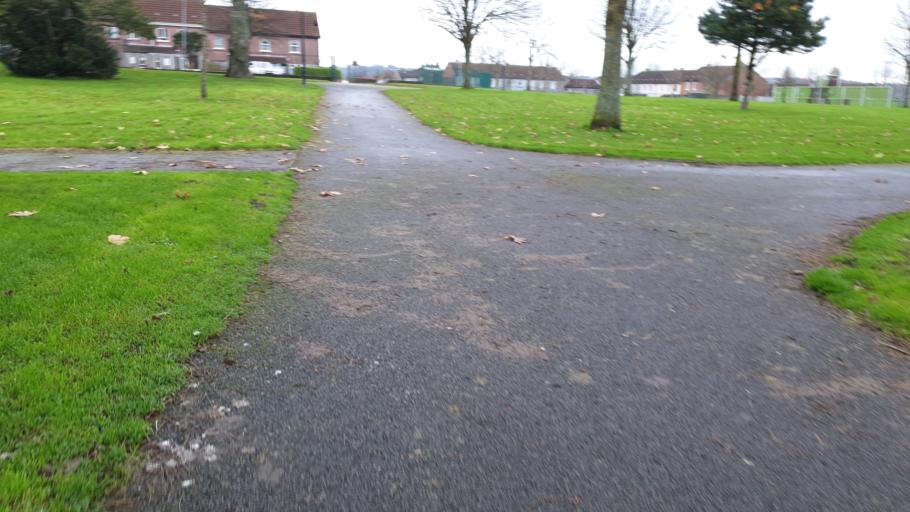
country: IE
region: Munster
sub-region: County Cork
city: Passage West
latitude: 51.8921
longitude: -8.3998
